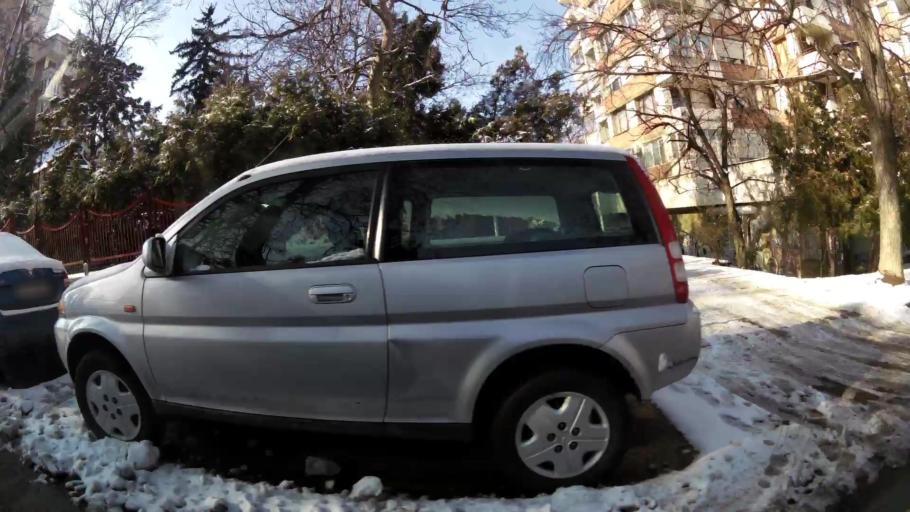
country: BG
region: Sofia-Capital
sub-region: Stolichna Obshtina
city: Sofia
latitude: 42.6767
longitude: 23.3216
